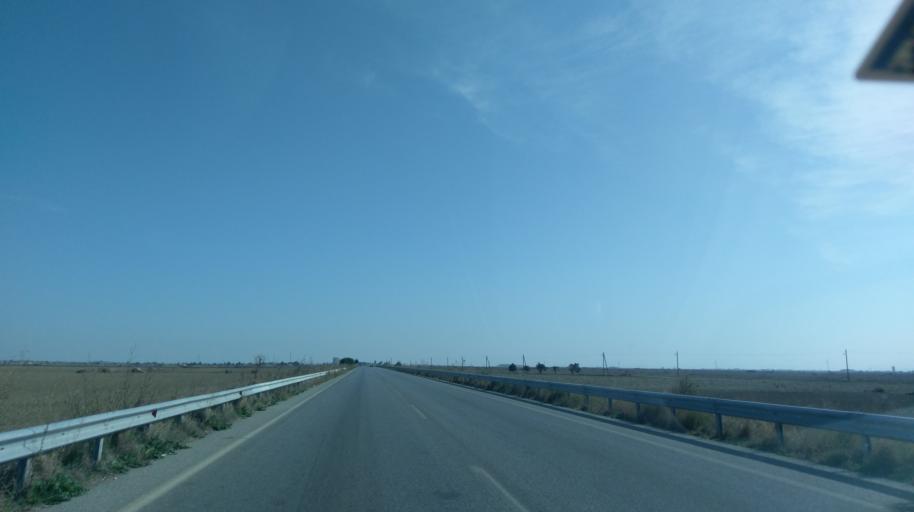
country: CY
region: Ammochostos
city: Lefkonoiko
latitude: 35.2568
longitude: 33.6943
